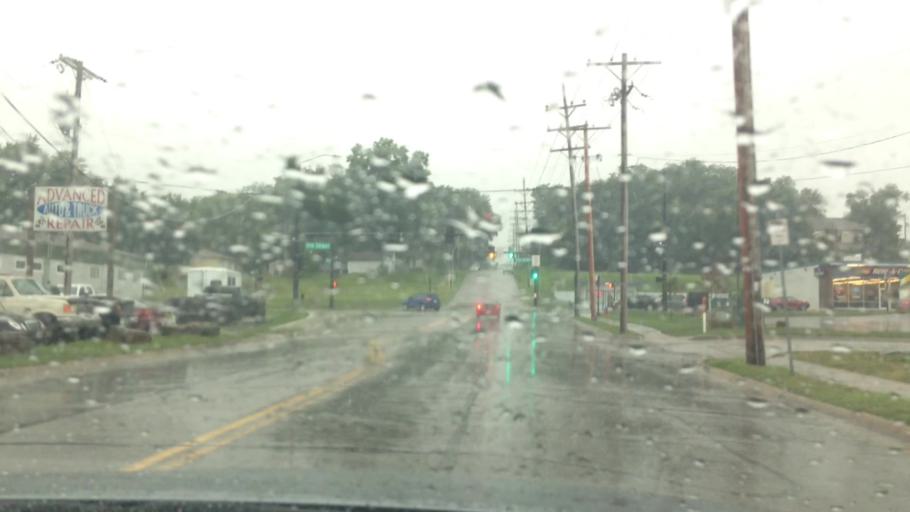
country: US
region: Kansas
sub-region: Leavenworth County
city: Leavenworth
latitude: 39.2951
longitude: -94.9079
